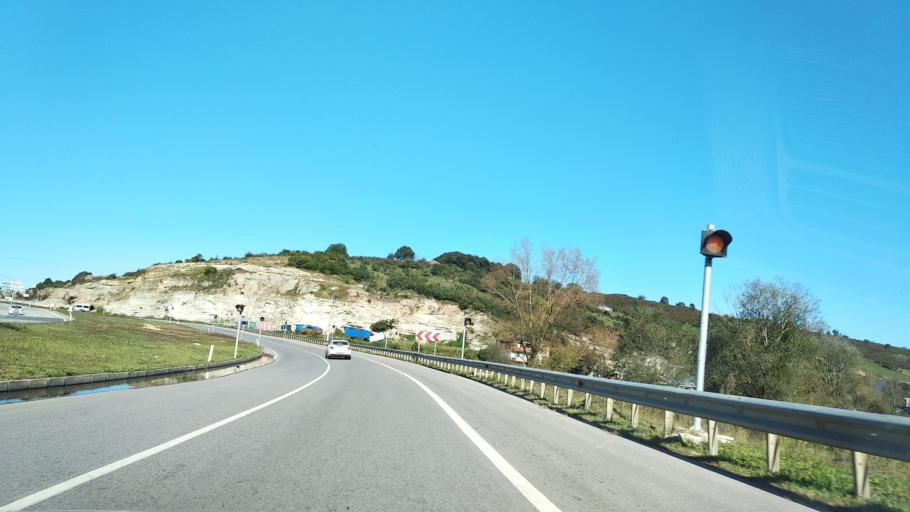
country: TR
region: Sakarya
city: Karasu
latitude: 41.0924
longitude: 30.6521
